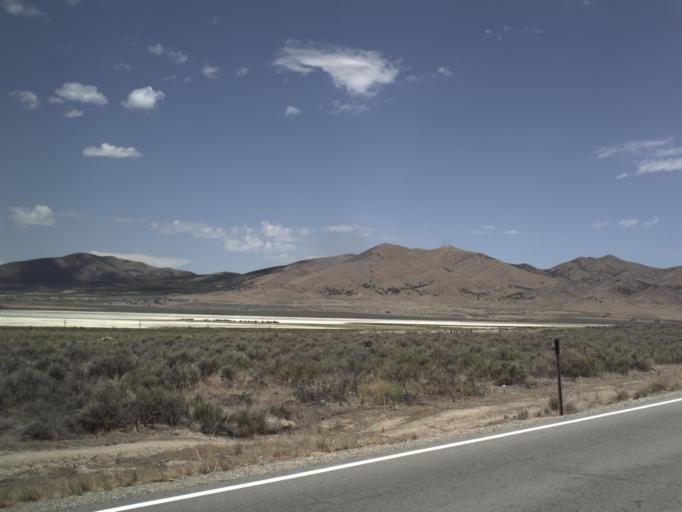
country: US
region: Utah
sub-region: Tooele County
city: Tooele
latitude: 40.4063
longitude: -112.3855
